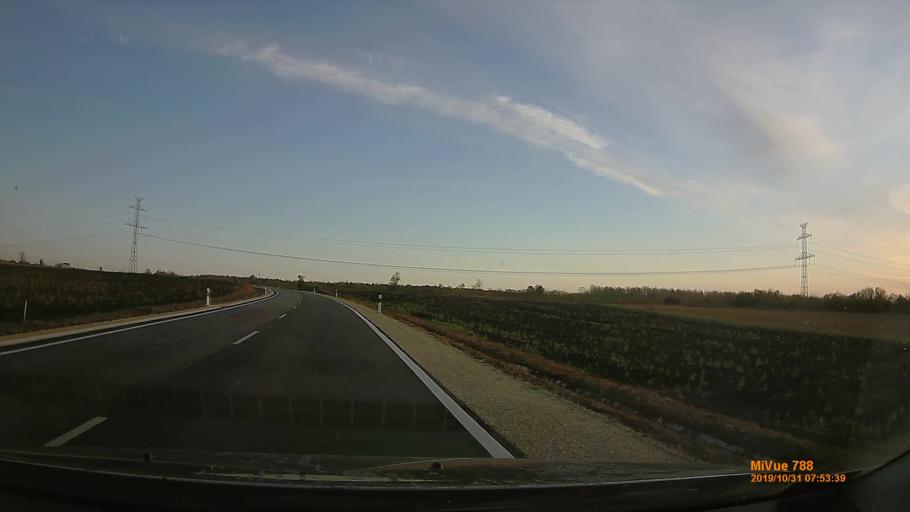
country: HU
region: Pest
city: Pilis
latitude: 47.3128
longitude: 19.5618
